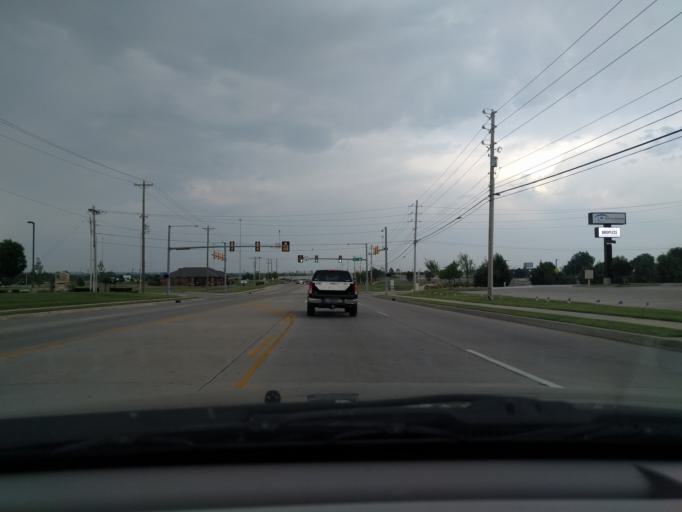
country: US
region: Oklahoma
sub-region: Tulsa County
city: Broken Arrow
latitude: 36.0464
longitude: -95.8652
